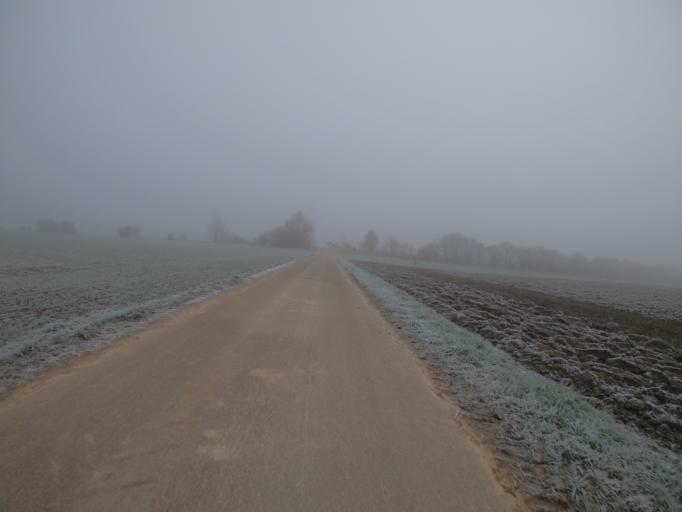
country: DE
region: Baden-Wuerttemberg
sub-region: Tuebingen Region
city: Beimerstetten
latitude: 48.4569
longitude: 9.9916
